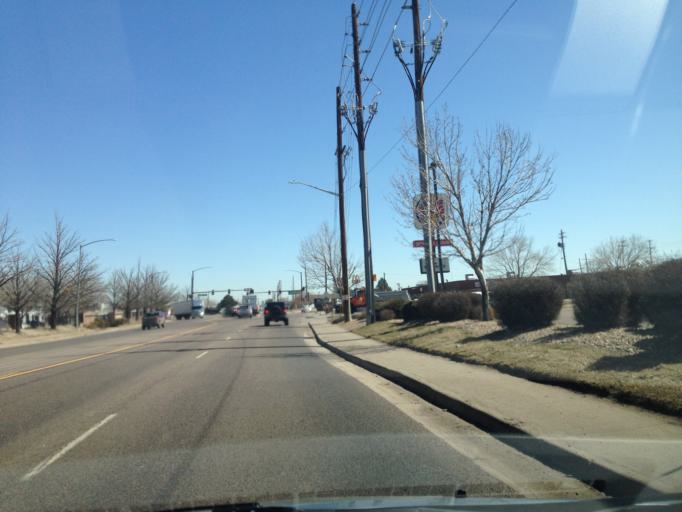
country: US
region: Colorado
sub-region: Adams County
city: Twin Lakes
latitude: 39.8018
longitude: -104.9804
